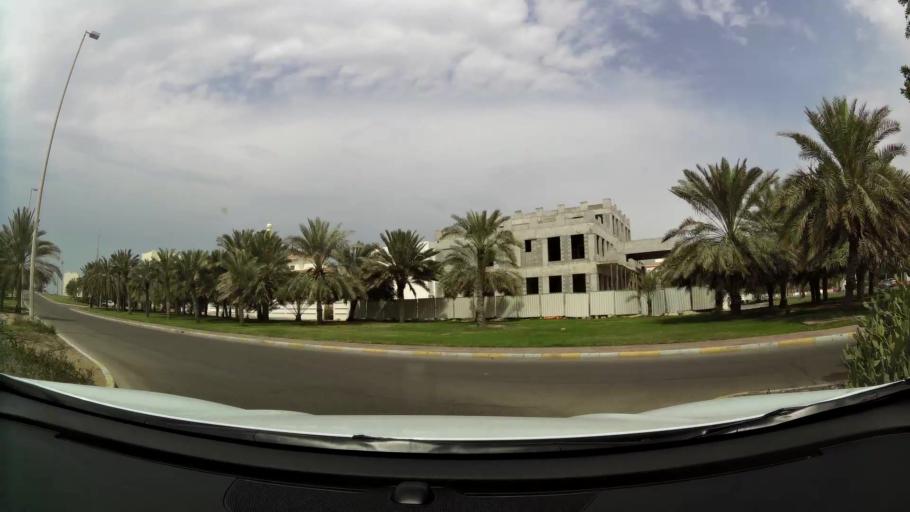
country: AE
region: Abu Dhabi
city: Abu Dhabi
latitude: 24.4611
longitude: 54.3371
